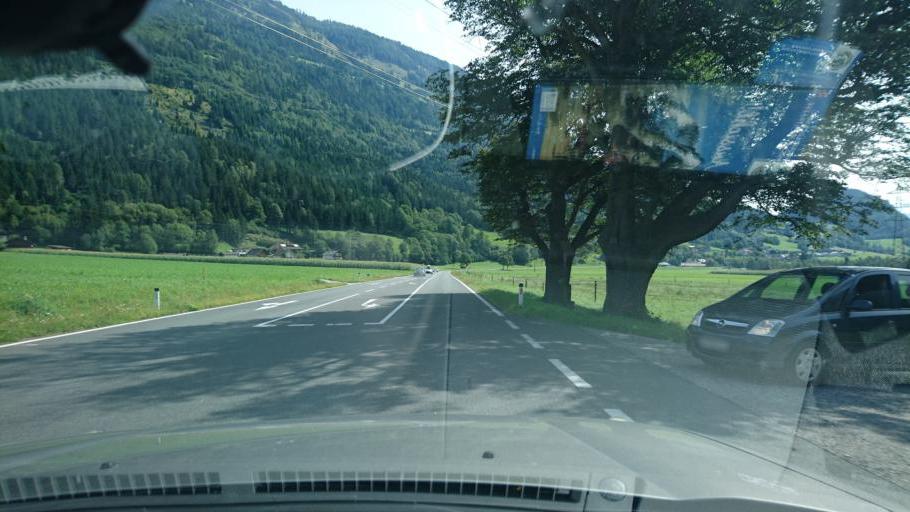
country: AT
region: Carinthia
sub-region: Politischer Bezirk Spittal an der Drau
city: Obervellach
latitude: 46.9072
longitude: 13.2491
